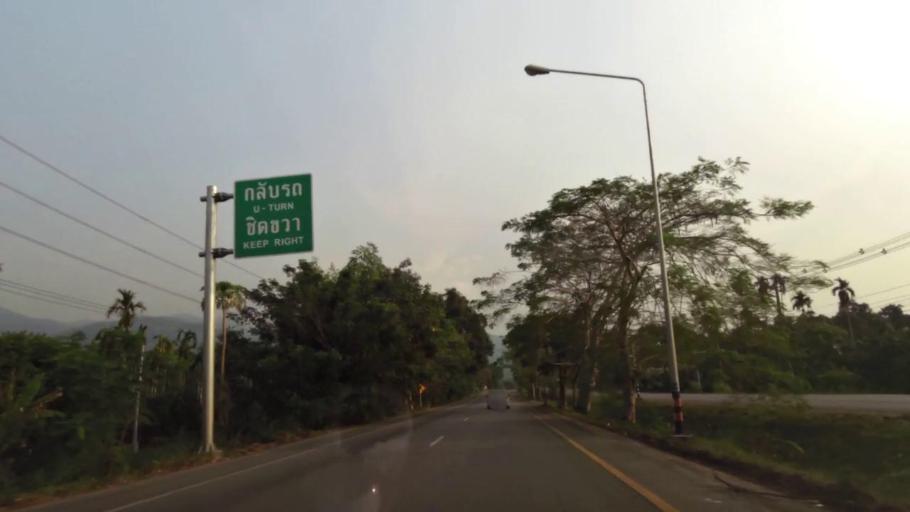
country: TH
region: Chanthaburi
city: Chanthaburi
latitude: 12.5859
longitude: 102.1564
